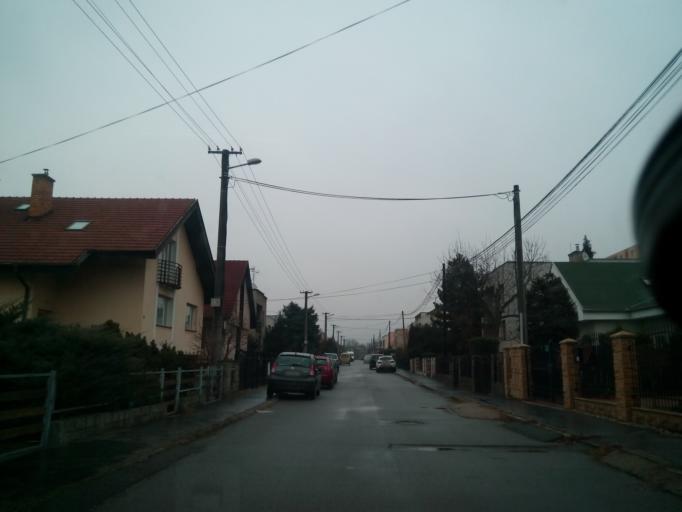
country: SK
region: Presovsky
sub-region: Okres Presov
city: Presov
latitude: 48.9732
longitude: 21.2590
